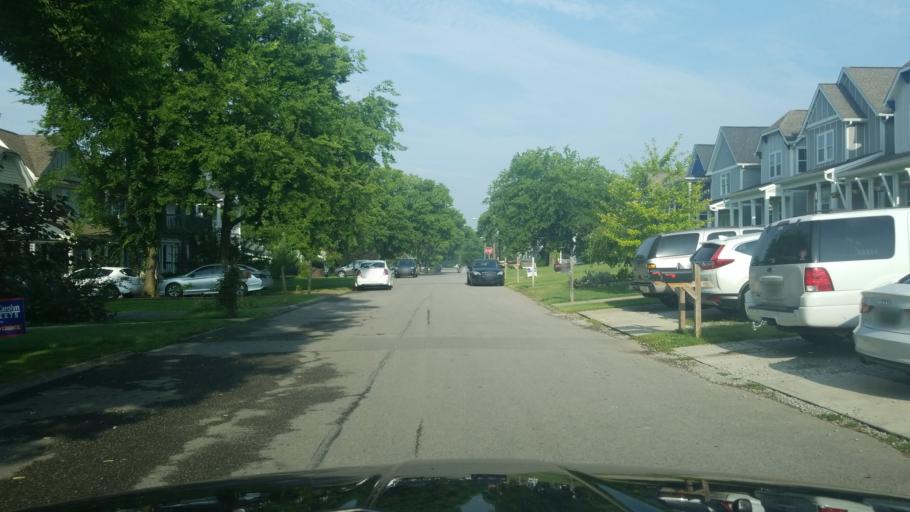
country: US
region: Tennessee
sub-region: Davidson County
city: Belle Meade
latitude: 36.1598
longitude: -86.8520
